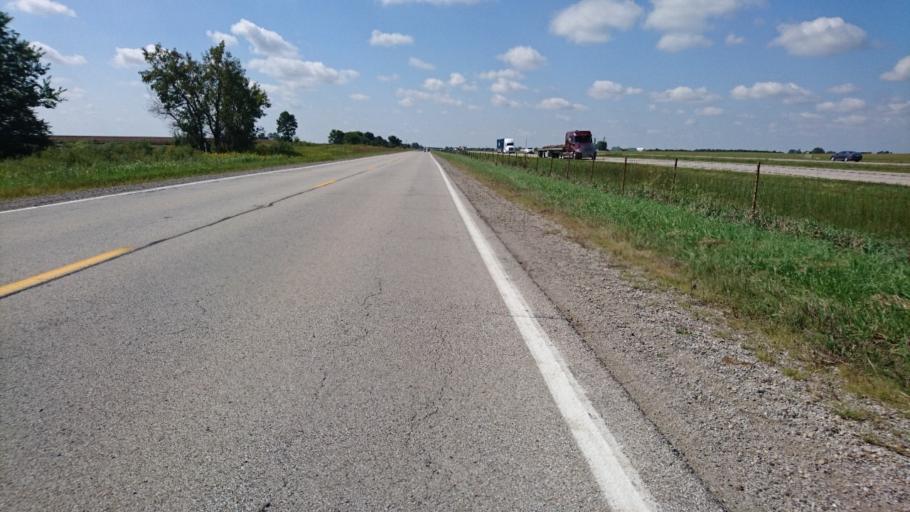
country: US
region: Illinois
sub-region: McLean County
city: Lexington
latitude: 40.6155
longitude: -88.8233
